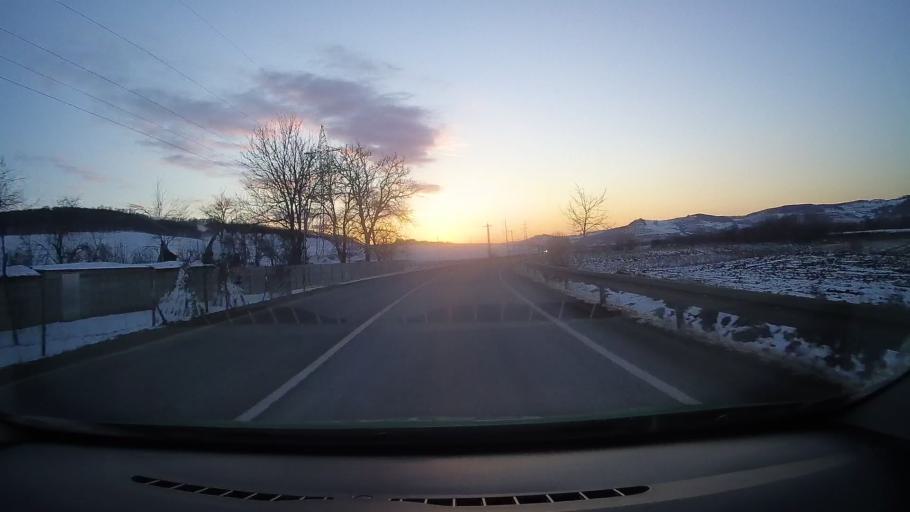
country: RO
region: Sibiu
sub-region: Comuna Alma
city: Alma
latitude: 46.1950
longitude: 24.4714
